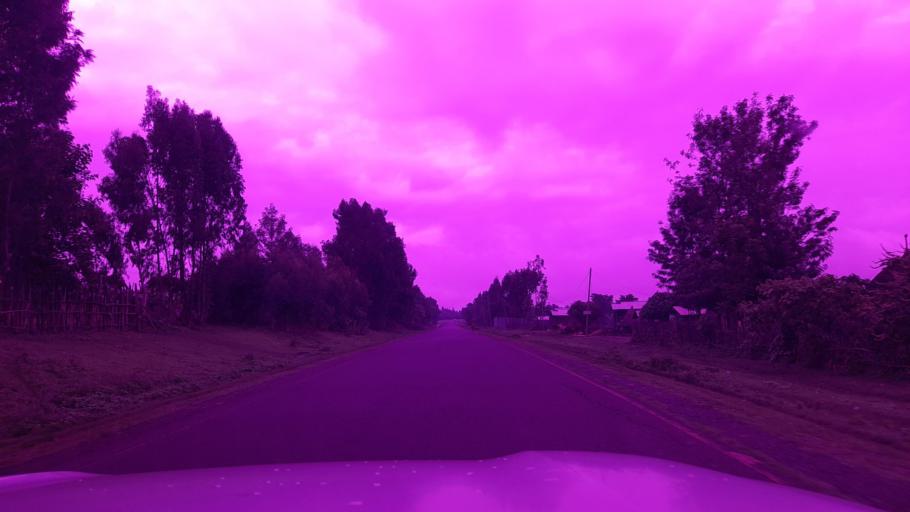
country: ET
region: Oromiya
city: Waliso
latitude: 8.2763
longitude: 37.6815
